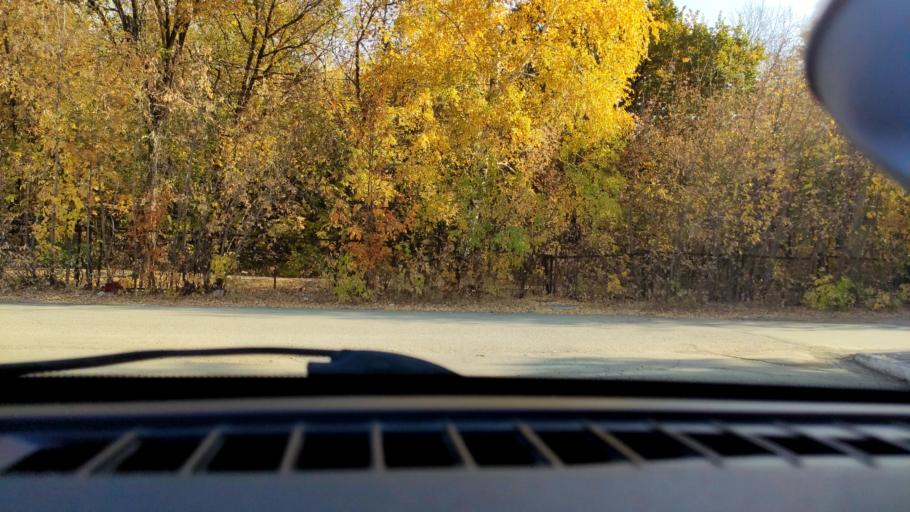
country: RU
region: Samara
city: Samara
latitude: 53.2232
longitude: 50.1642
